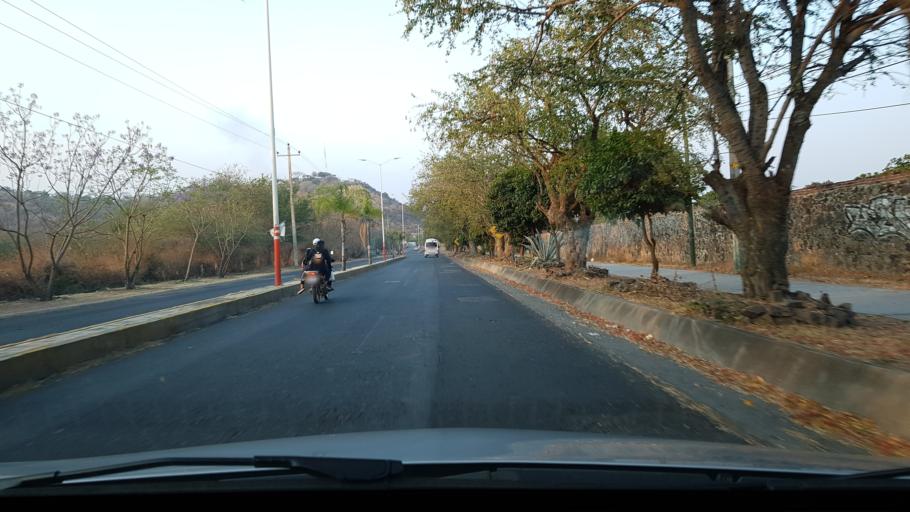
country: MX
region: Morelos
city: Jonacatepec de Leandro Valle
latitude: 18.6719
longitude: -98.8054
